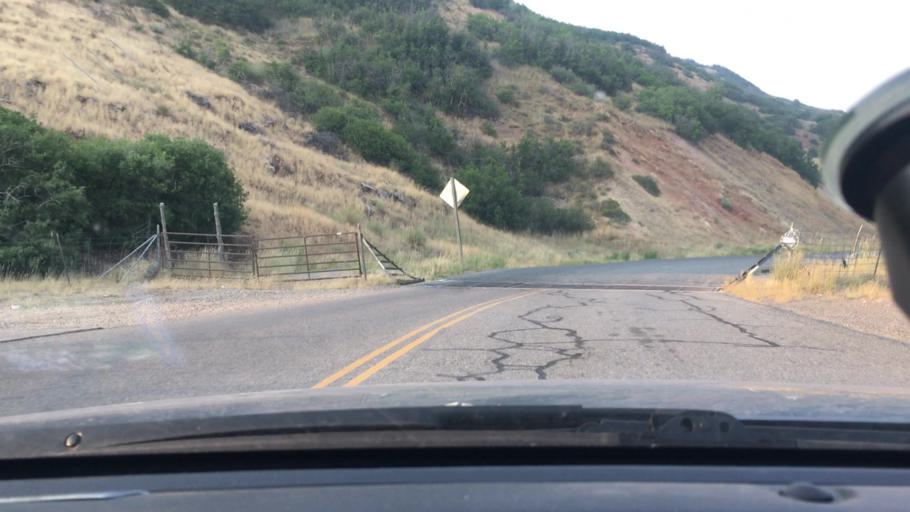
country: US
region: Utah
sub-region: Utah County
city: Mapleton
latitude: 40.0293
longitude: -111.5051
